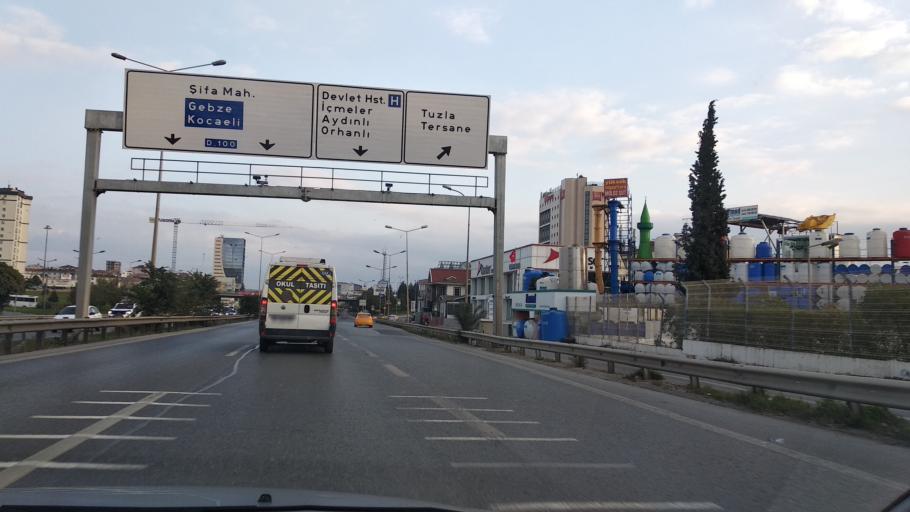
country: TR
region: Istanbul
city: Icmeler
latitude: 40.8515
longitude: 29.2957
